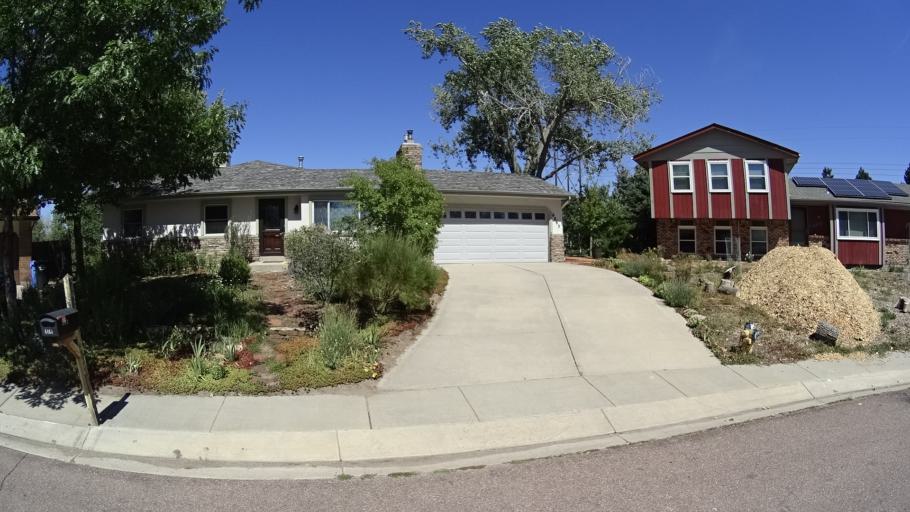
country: US
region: Colorado
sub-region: El Paso County
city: Colorado Springs
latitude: 38.9286
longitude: -104.7851
